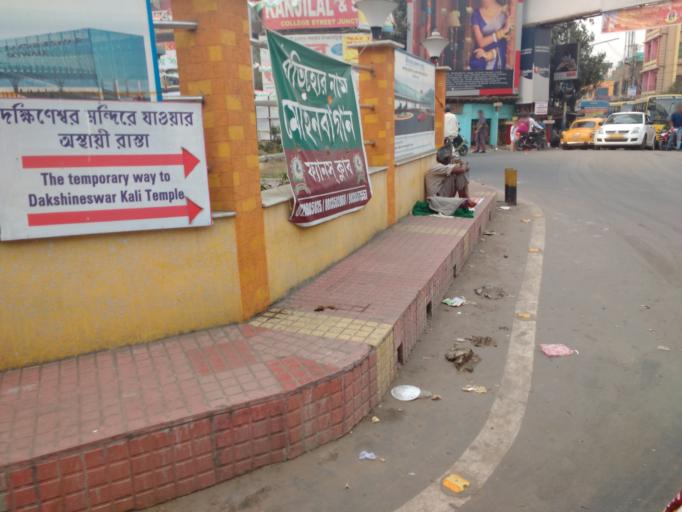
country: IN
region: West Bengal
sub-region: North 24 Parganas
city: Baranagar
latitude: 22.6538
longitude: 88.3621
